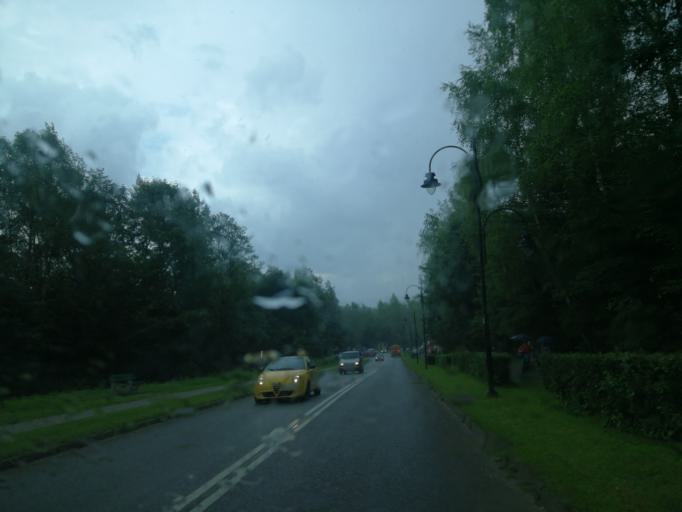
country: PL
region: Subcarpathian Voivodeship
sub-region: Powiat leski
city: Polanczyk
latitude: 49.3787
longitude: 22.4446
